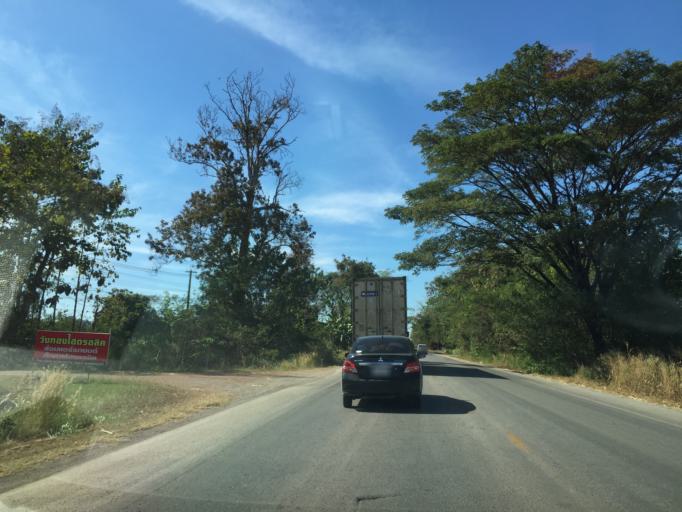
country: TH
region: Changwat Nong Bua Lamphu
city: Na Klang
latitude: 17.3208
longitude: 102.1459
